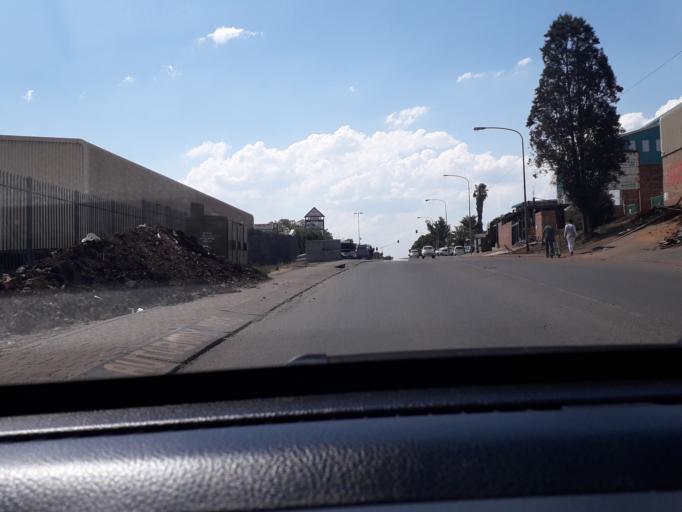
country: ZA
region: Gauteng
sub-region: City of Tshwane Metropolitan Municipality
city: Centurion
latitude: -25.8409
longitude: 28.2158
